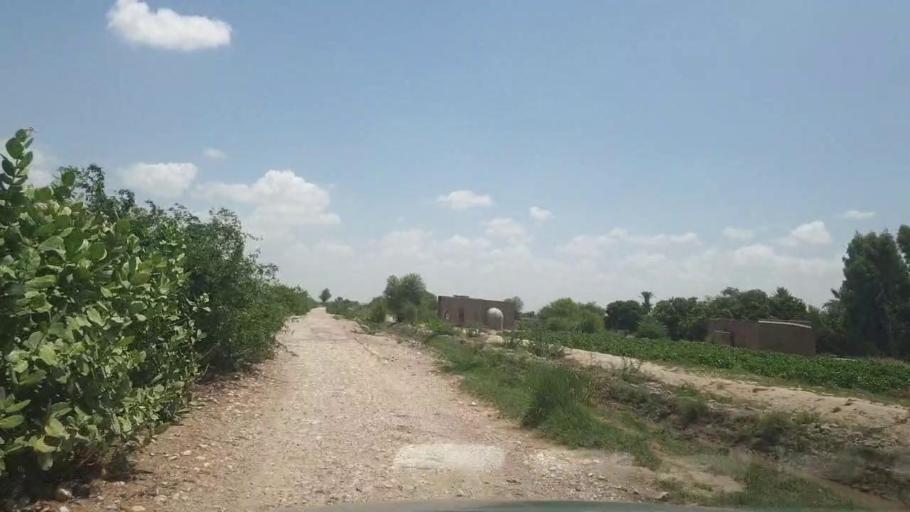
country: PK
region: Sindh
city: Kot Diji
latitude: 27.2927
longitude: 69.0819
